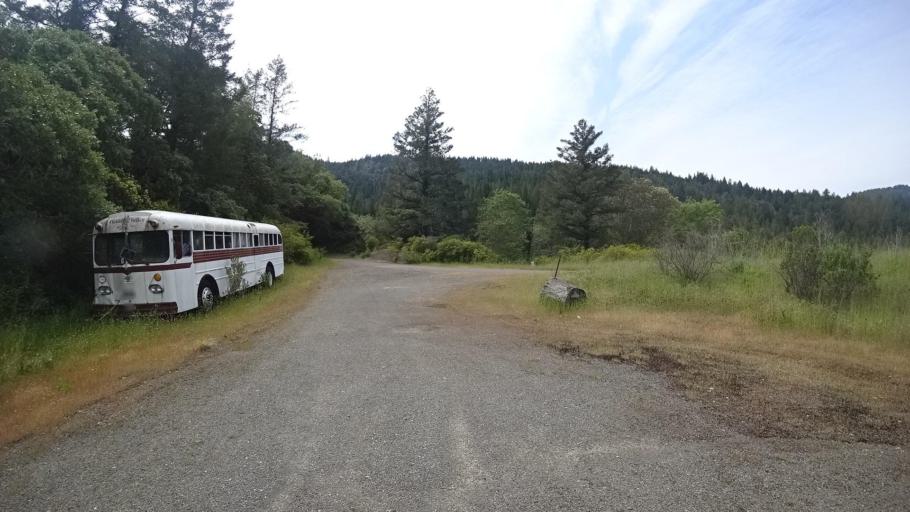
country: US
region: California
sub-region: Humboldt County
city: Redway
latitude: 40.0309
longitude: -123.7794
